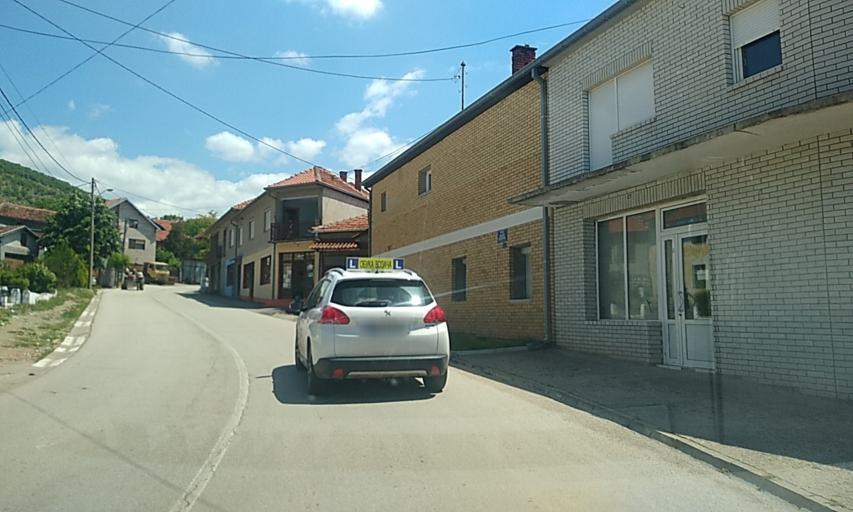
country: RS
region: Central Serbia
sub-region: Nisavski Okrug
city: Nis
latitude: 43.3637
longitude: 21.9679
